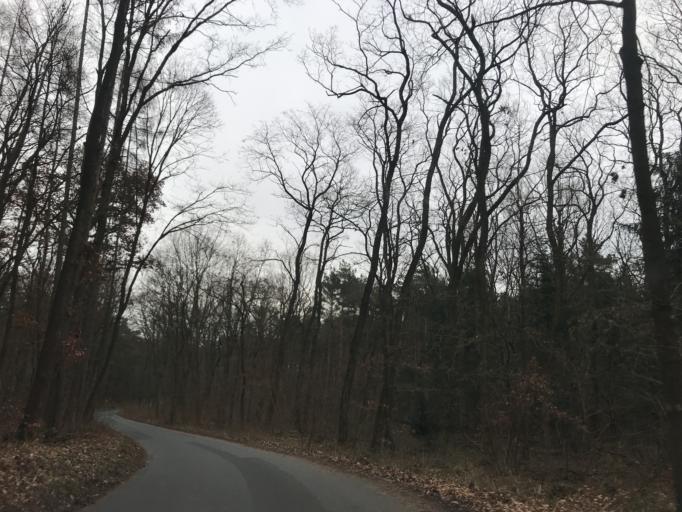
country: DE
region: Berlin
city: Kladow
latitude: 52.4803
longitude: 13.1450
